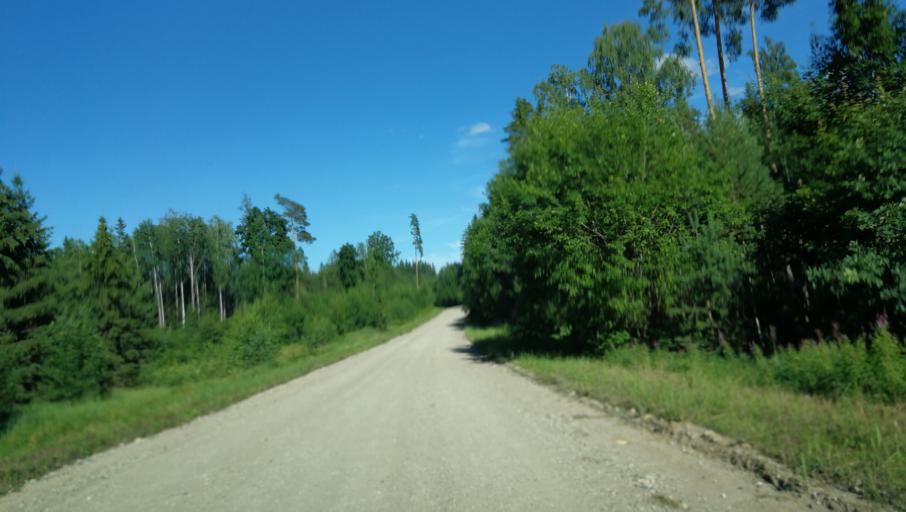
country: LV
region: Jaunpiebalga
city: Jaunpiebalga
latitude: 56.9944
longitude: 26.0159
